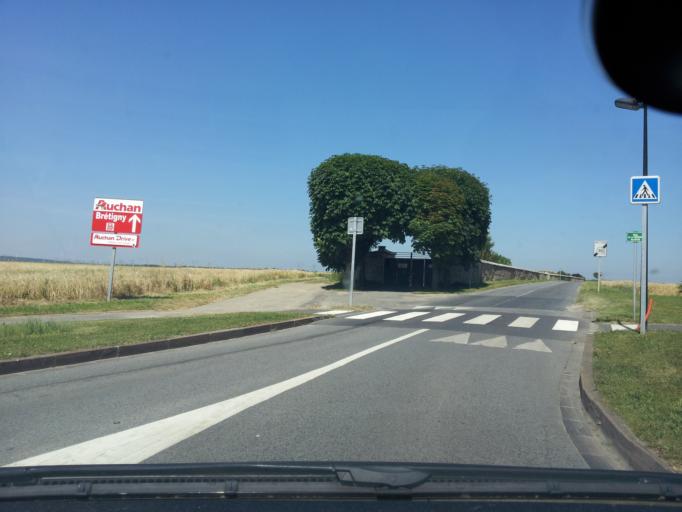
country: FR
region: Ile-de-France
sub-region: Departement de l'Essonne
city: Vert-le-Petit
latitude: 48.5537
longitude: 2.3629
